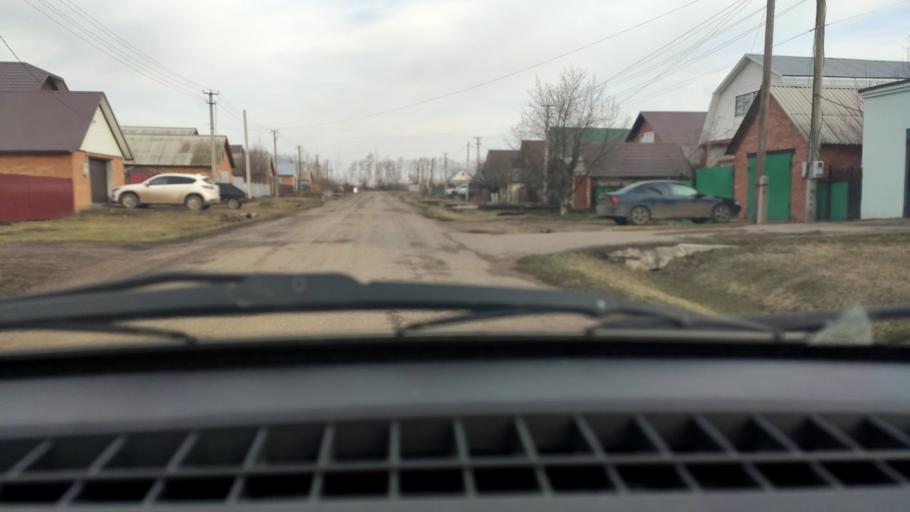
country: RU
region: Bashkortostan
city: Davlekanovo
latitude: 54.2322
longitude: 55.0286
